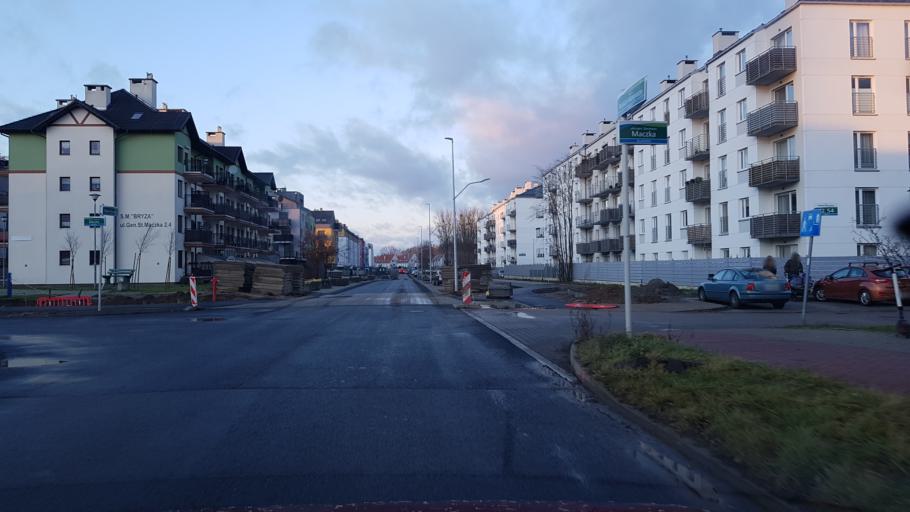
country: PL
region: West Pomeranian Voivodeship
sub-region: Powiat policki
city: Przeclaw
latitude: 53.4286
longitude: 14.4872
